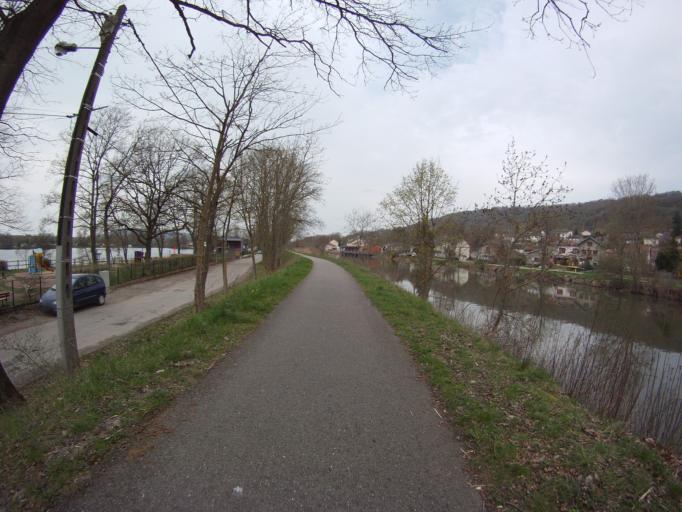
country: FR
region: Lorraine
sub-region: Departement de Meurthe-et-Moselle
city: Messein
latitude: 48.6090
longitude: 6.1476
